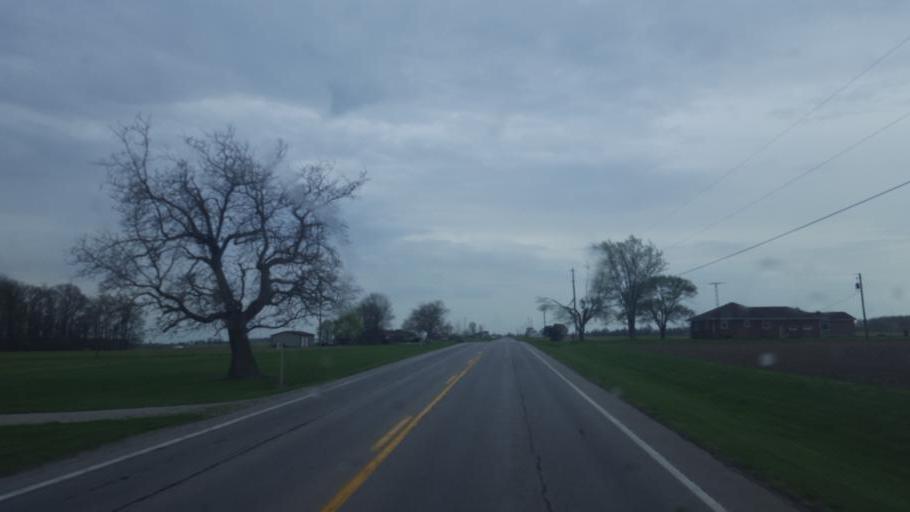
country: US
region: Ohio
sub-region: Wyandot County
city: Carey
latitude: 41.0443
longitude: -83.4016
